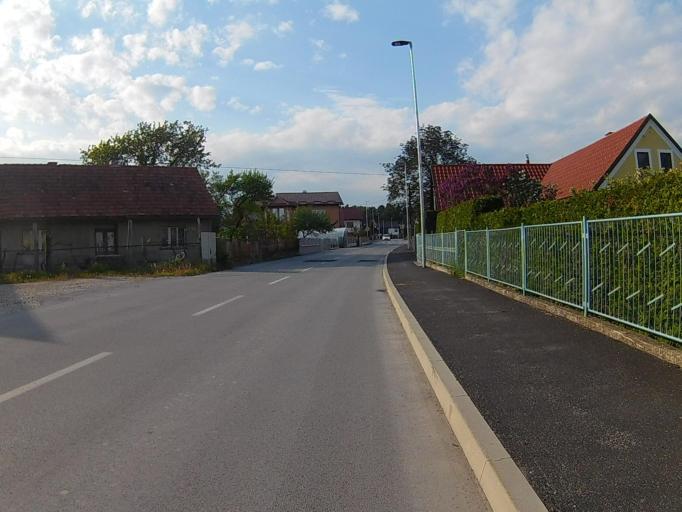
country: SI
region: Miklavz na Dravskem Polju
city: Miklavz na Dravskem Polju
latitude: 46.4823
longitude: 15.7017
